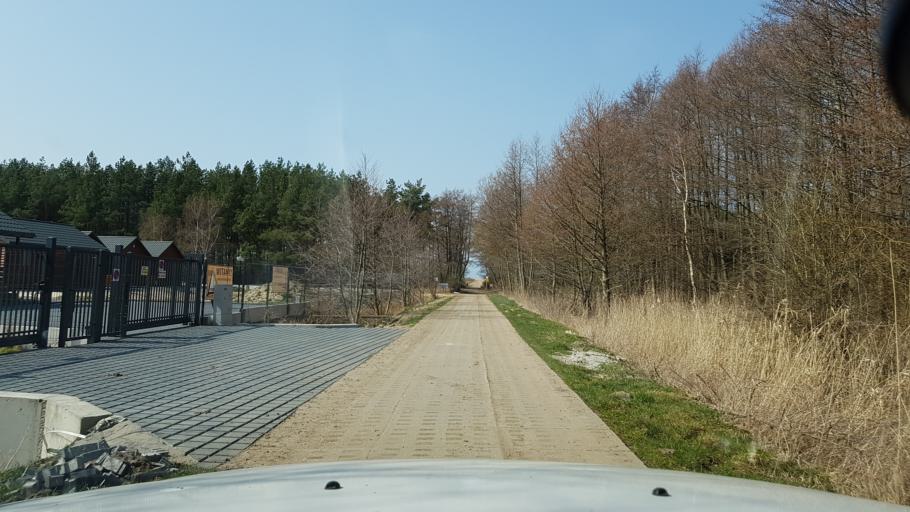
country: PL
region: West Pomeranian Voivodeship
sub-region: Powiat slawienski
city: Darlowo
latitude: 54.4635
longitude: 16.4133
